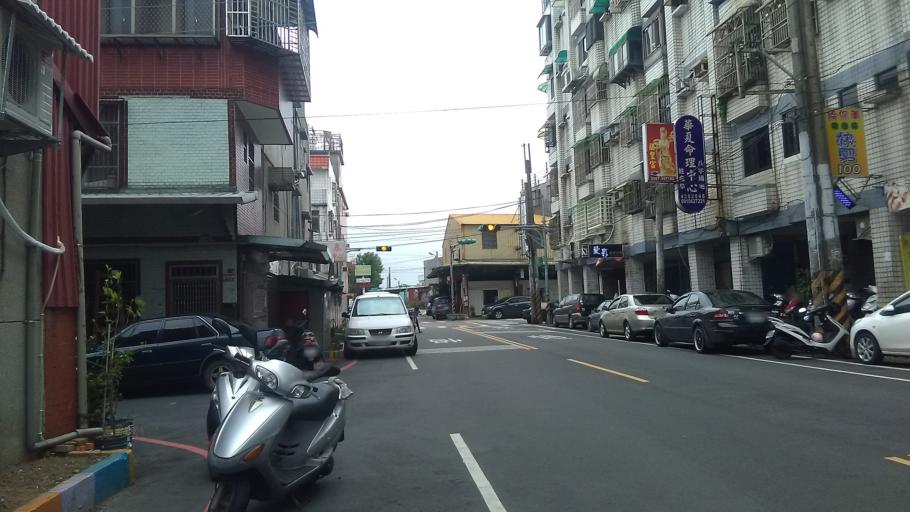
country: TW
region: Taiwan
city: Taoyuan City
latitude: 24.9503
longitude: 121.2619
